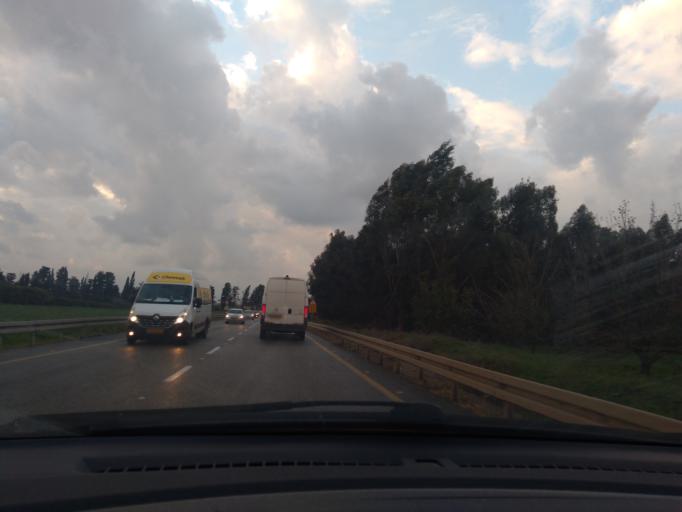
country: IL
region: Central District
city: Elyakhin
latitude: 32.3763
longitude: 34.8988
